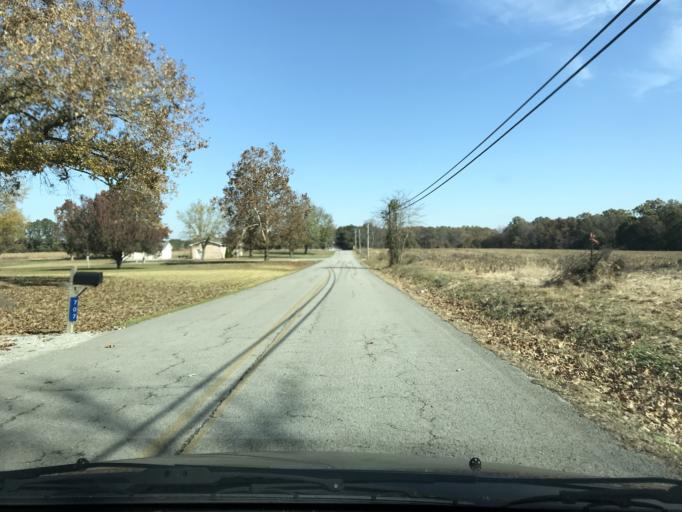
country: US
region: Tennessee
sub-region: Coffee County
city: Tullahoma
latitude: 35.3990
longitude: -86.1619
